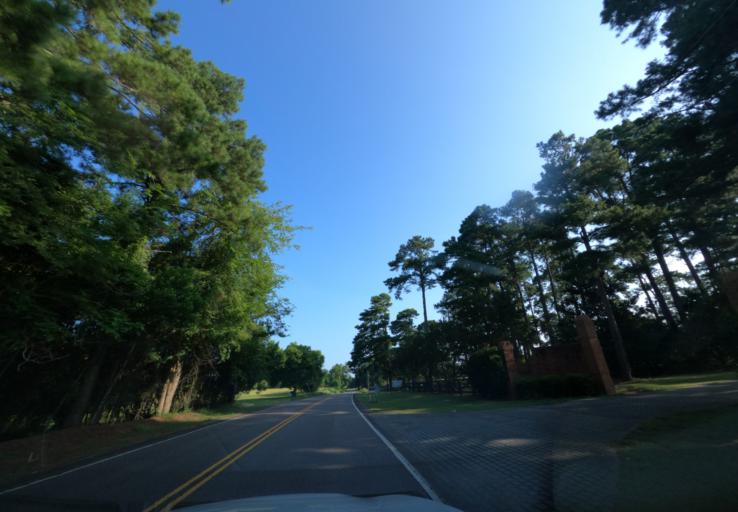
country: US
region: South Carolina
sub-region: Edgefield County
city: Murphys Estates
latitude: 33.6178
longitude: -81.9678
